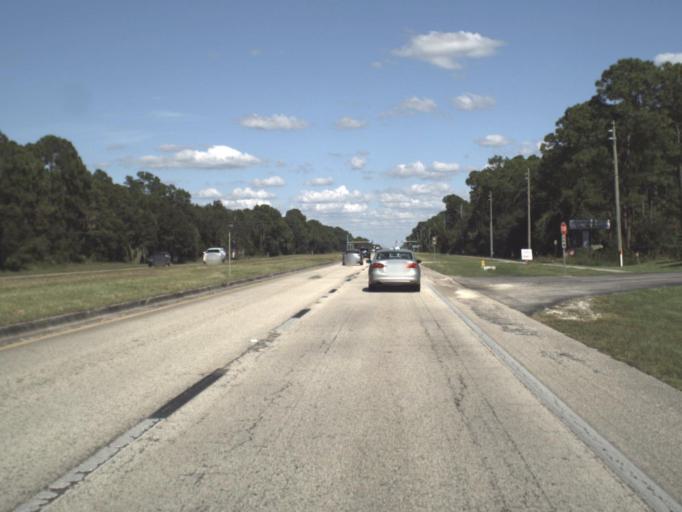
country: US
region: Florida
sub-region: Sarasota County
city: North Port
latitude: 27.0016
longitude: -82.1788
